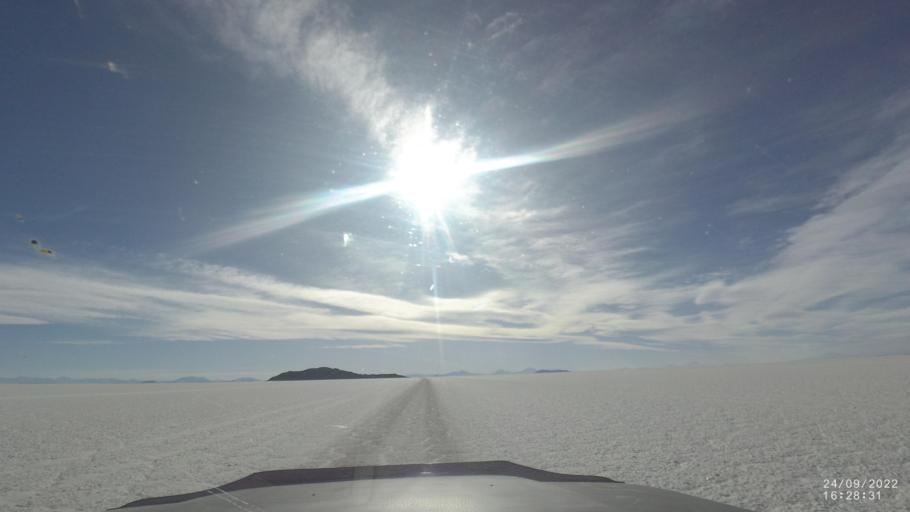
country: BO
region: Potosi
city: Colchani
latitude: -20.2419
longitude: -67.6007
